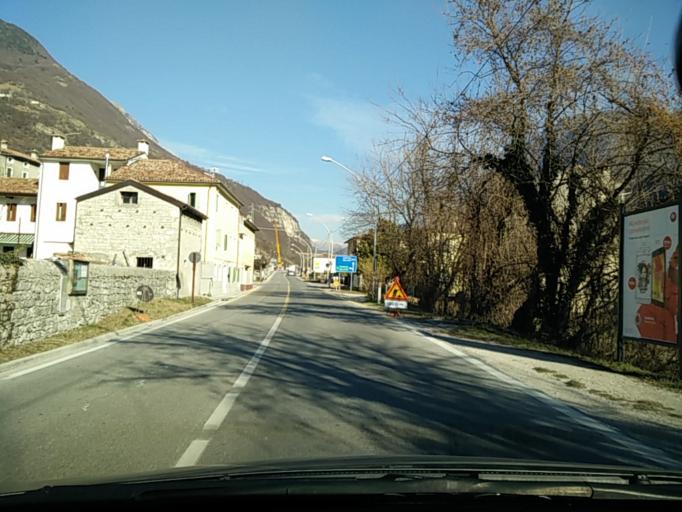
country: IT
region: Veneto
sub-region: Provincia di Treviso
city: Revine
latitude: 46.0181
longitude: 12.2901
